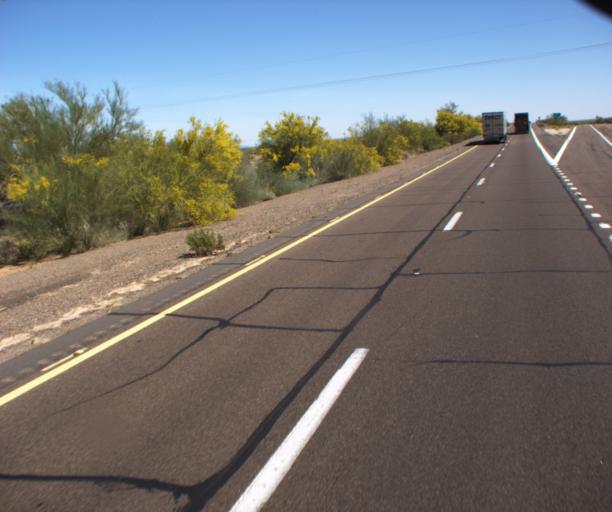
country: US
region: Arizona
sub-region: Yuma County
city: Wellton
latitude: 32.8239
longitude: -113.4473
